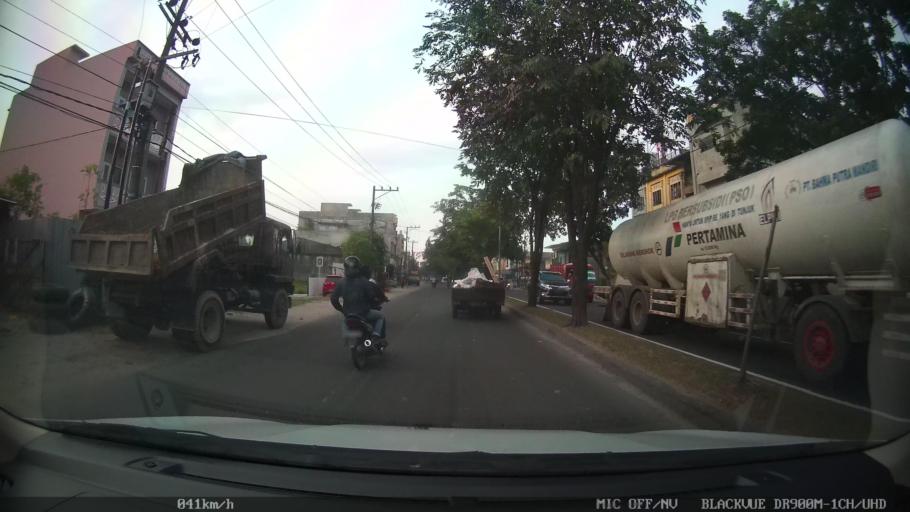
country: ID
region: North Sumatra
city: Sunggal
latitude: 3.5726
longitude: 98.6101
